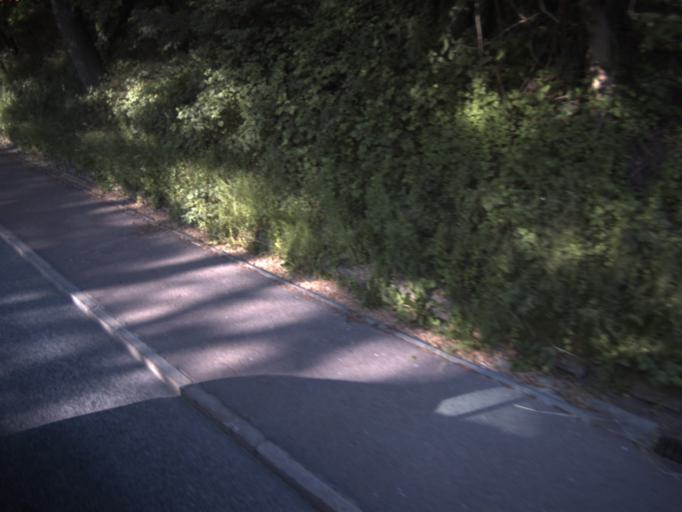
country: SE
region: Skane
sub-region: Helsingborg
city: Helsingborg
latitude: 56.0768
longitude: 12.6657
